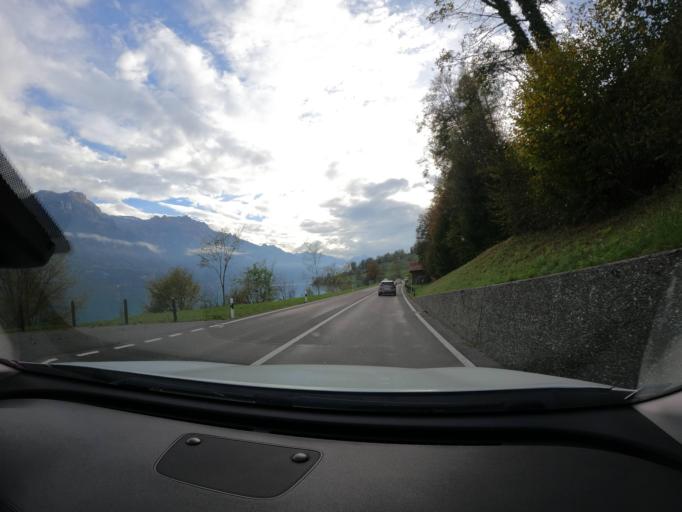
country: CH
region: Bern
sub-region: Interlaken-Oberhasli District
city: Brienz
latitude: 46.7466
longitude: 7.9773
